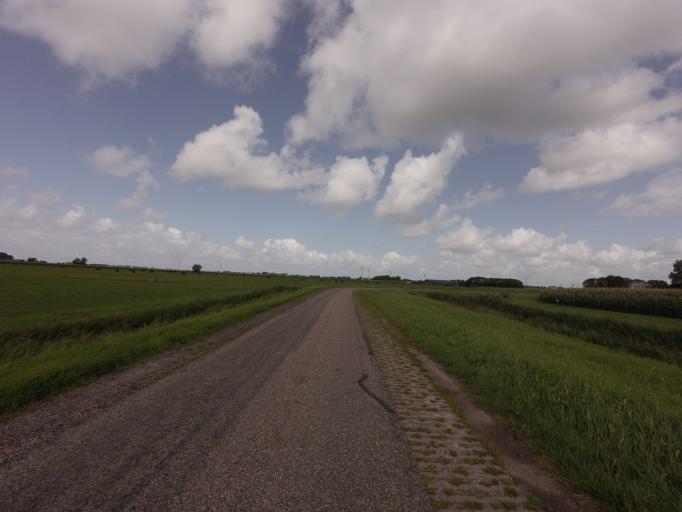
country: NL
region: Friesland
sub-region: Gemeente Franekeradeel
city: Sexbierum
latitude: 53.1692
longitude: 5.4860
